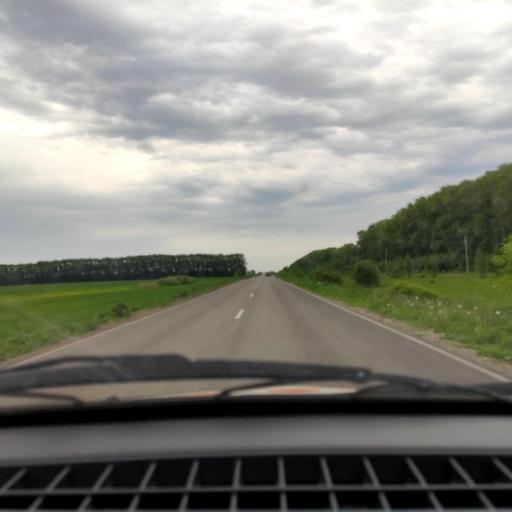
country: RU
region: Bashkortostan
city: Avdon
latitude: 54.5291
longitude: 55.7669
